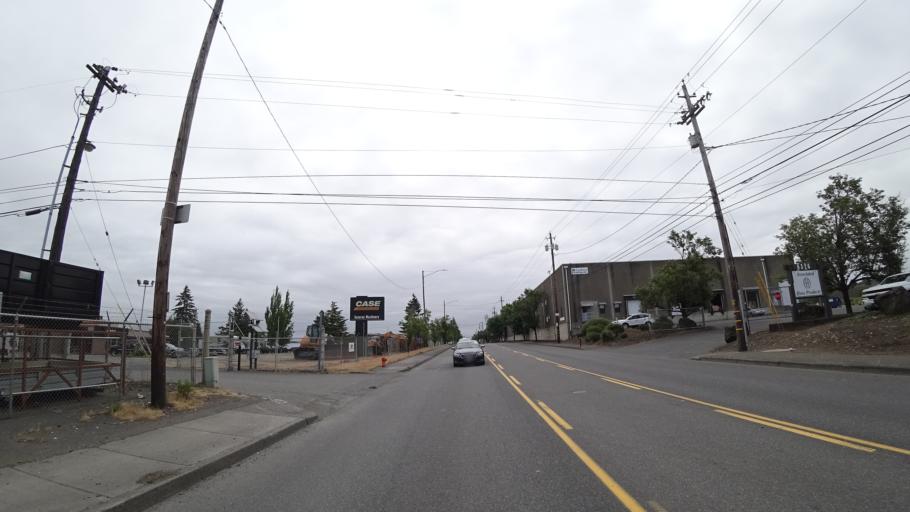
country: US
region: Oregon
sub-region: Multnomah County
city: Portland
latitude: 45.5683
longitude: -122.5976
